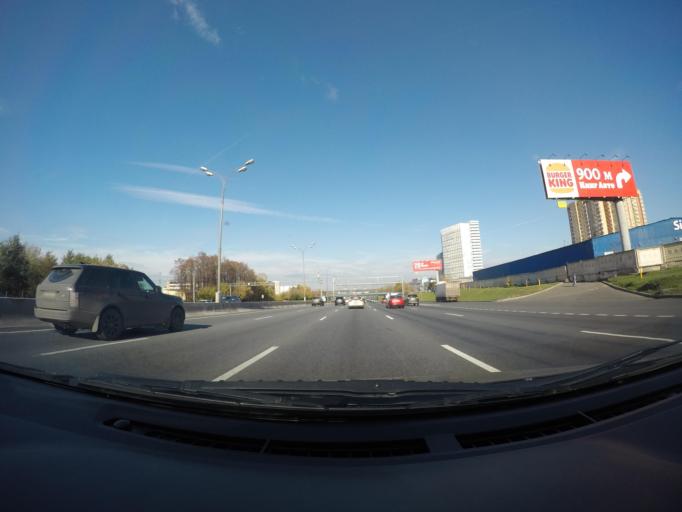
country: RU
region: Moscow
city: Vostochnyy
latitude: 55.8046
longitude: 37.8399
